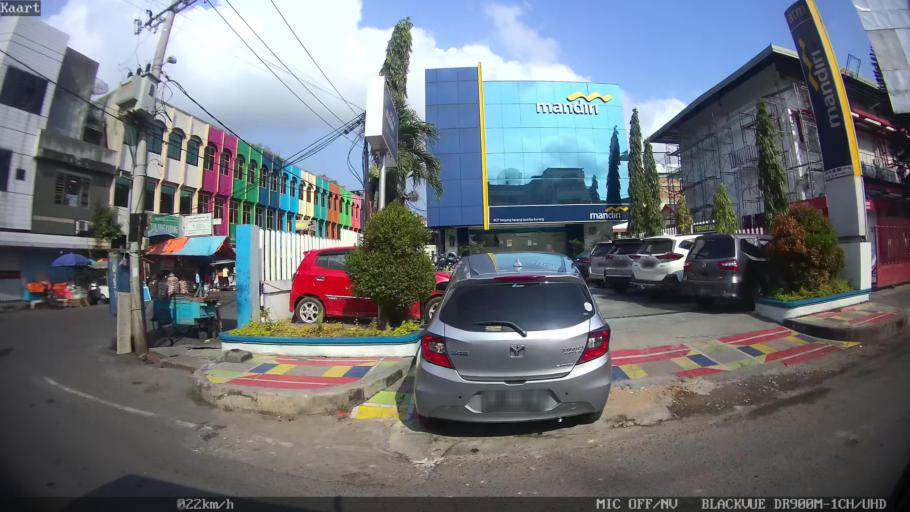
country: ID
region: Lampung
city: Bandarlampung
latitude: -5.4114
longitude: 105.2564
